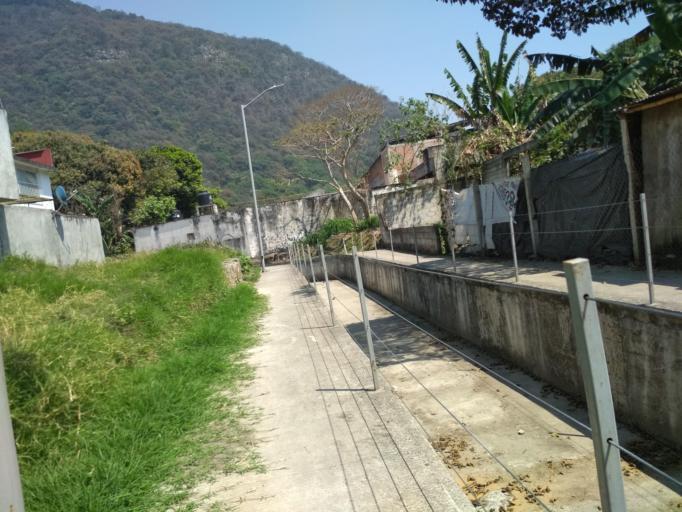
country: MX
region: Veracruz
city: Rio Blanco
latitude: 18.8431
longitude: -97.1233
